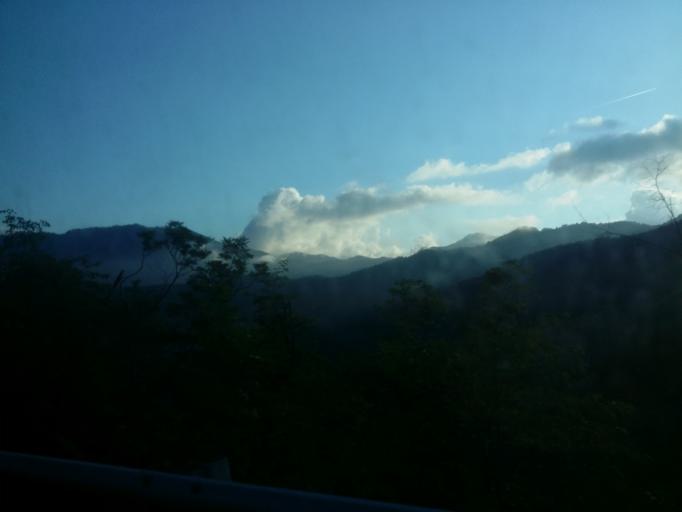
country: IT
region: Liguria
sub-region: Provincia di Genova
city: Borzonasca
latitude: 44.4699
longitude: 9.3685
